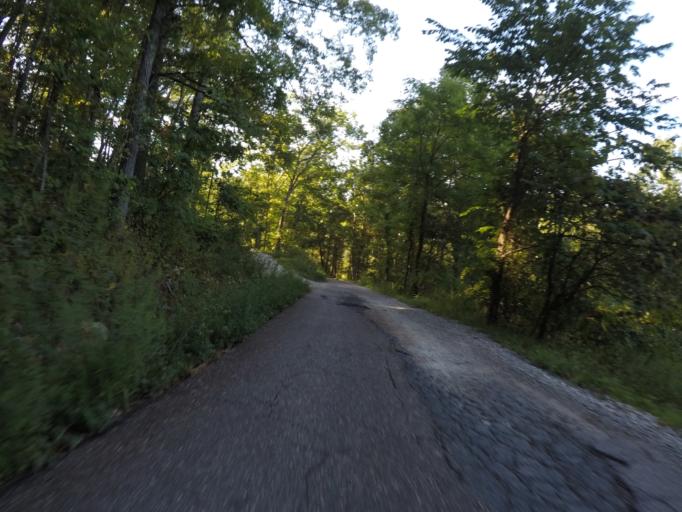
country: US
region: Ohio
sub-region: Lawrence County
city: Coal Grove
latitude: 38.5830
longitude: -82.5487
